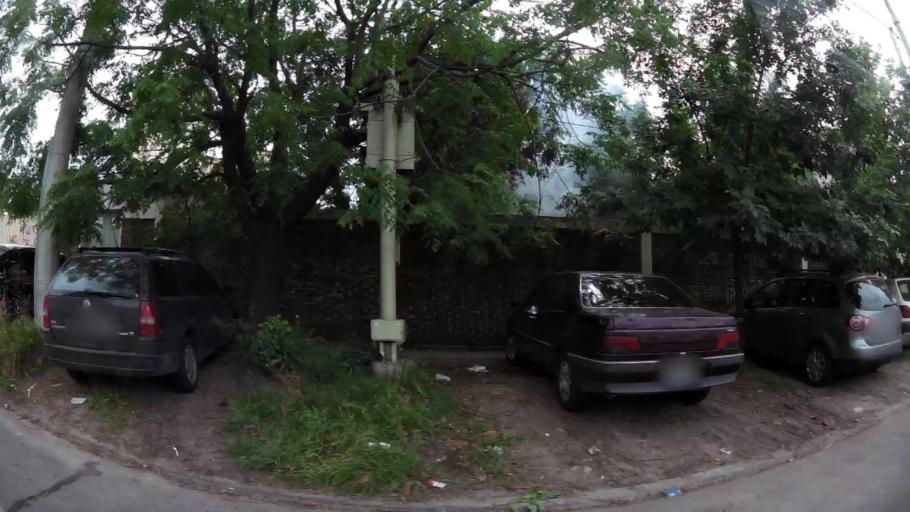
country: AR
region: Buenos Aires F.D.
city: Villa Lugano
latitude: -34.6880
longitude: -58.5119
